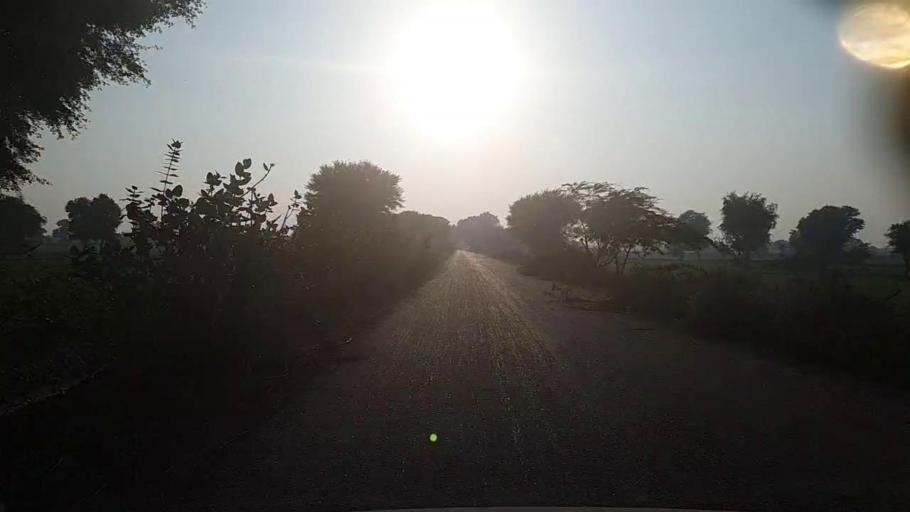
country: PK
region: Sindh
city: Pad Idan
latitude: 26.7165
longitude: 68.4025
